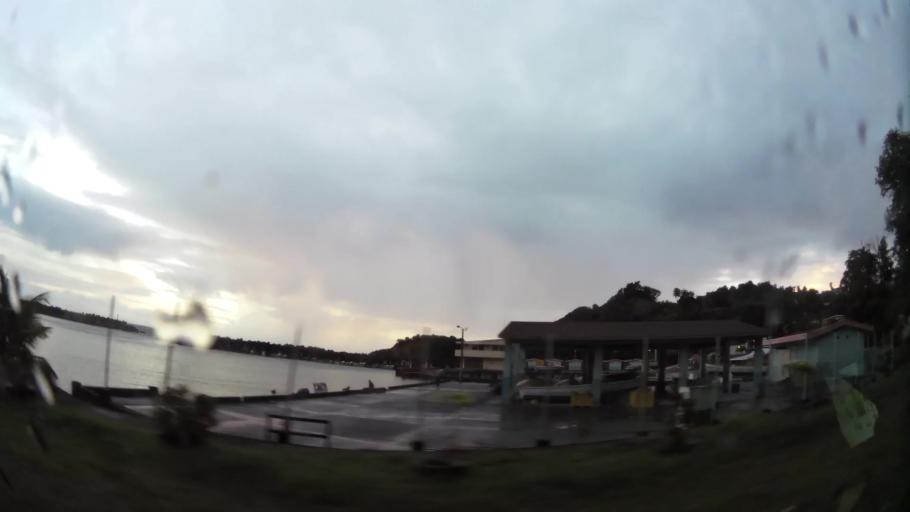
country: DM
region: Saint Andrew
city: Marigot
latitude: 15.5412
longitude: -61.2876
